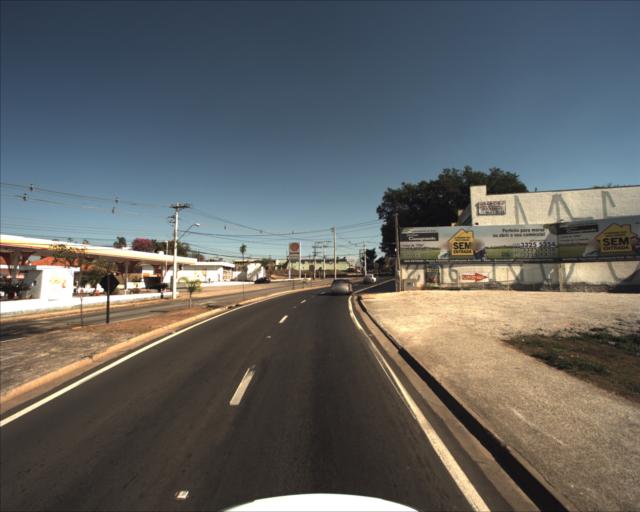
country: BR
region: Sao Paulo
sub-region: Sorocaba
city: Sorocaba
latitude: -23.4172
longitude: -47.4079
